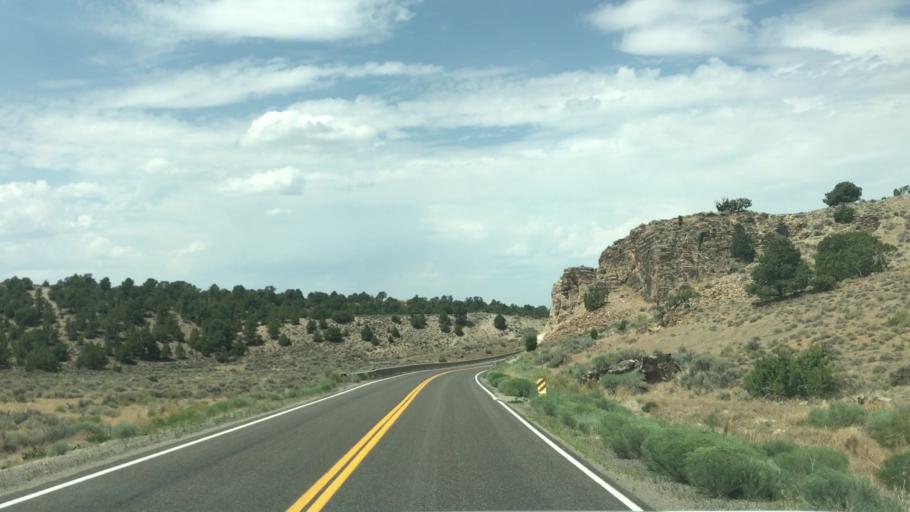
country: US
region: Nevada
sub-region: Eureka County
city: Eureka
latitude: 39.3912
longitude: -115.5007
